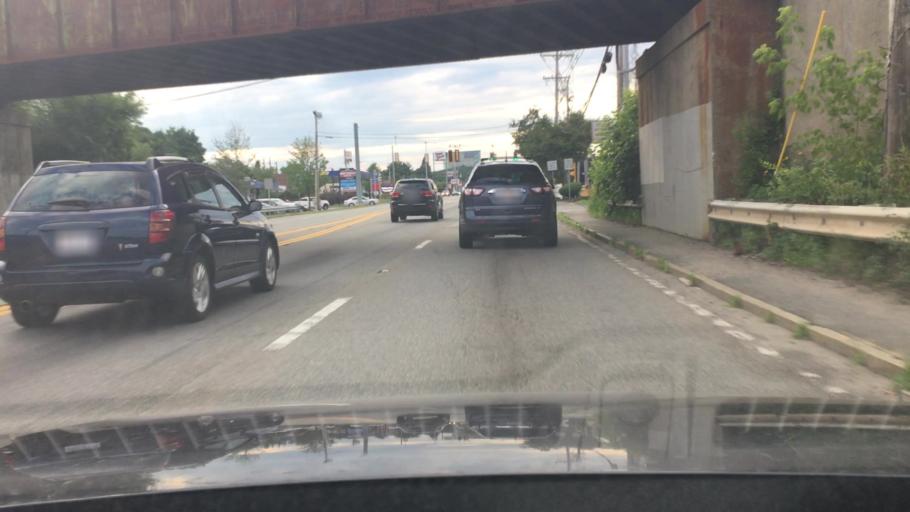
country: US
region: Massachusetts
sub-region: Essex County
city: Danvers
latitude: 42.5562
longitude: -70.9670
